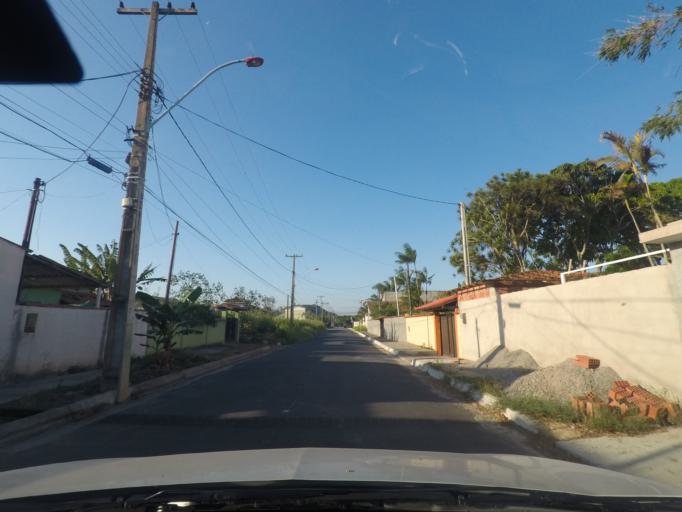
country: BR
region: Rio de Janeiro
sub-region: Marica
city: Marica
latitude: -22.9575
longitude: -42.9334
